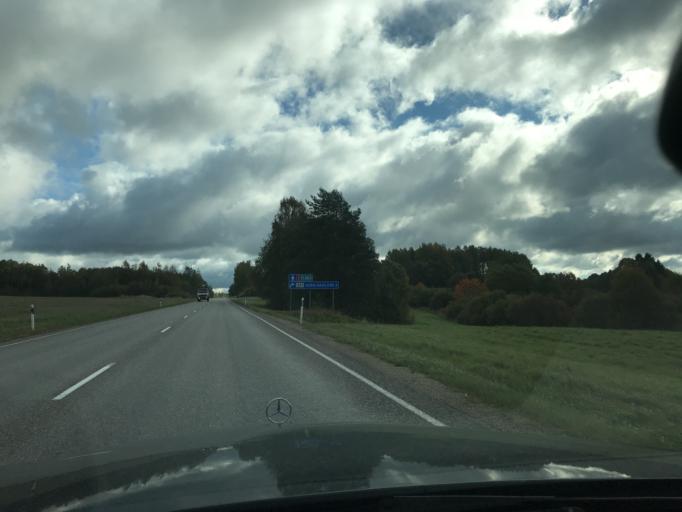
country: EE
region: Vorumaa
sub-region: Voru linn
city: Voru
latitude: 57.7595
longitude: 27.2091
